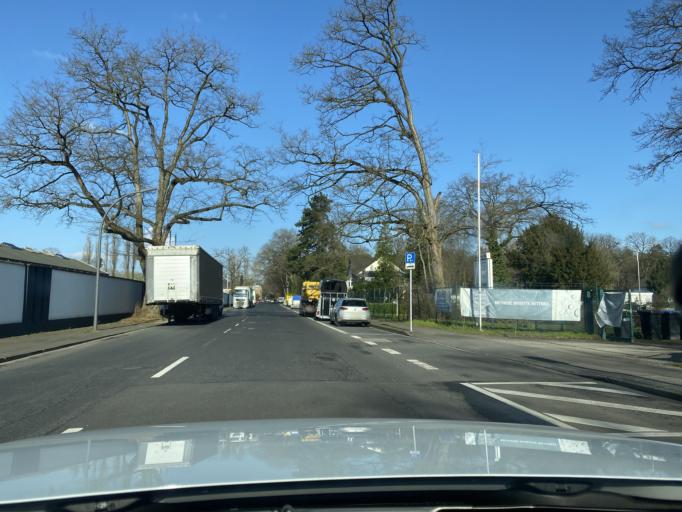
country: DE
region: North Rhine-Westphalia
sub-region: Regierungsbezirk Koln
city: Merheim
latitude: 50.9845
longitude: 7.0724
